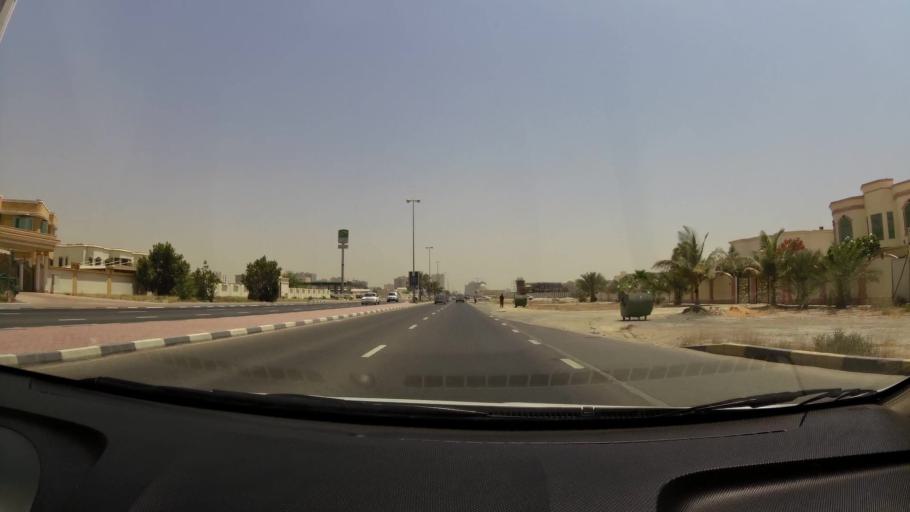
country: AE
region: Ajman
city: Ajman
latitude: 25.4168
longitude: 55.5126
